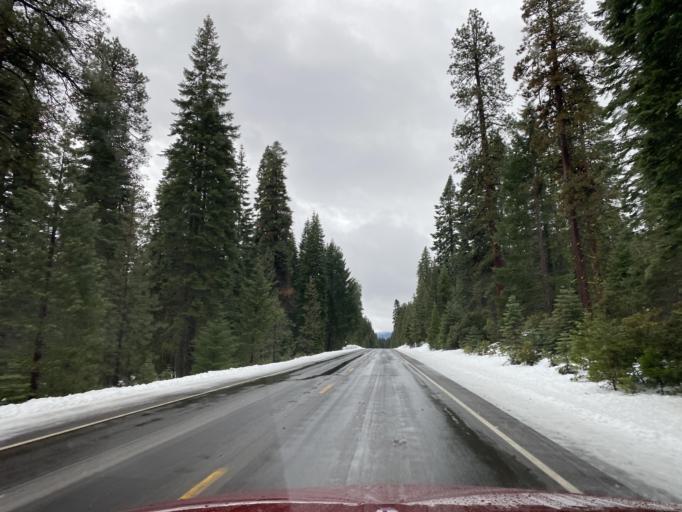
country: US
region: Oregon
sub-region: Klamath County
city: Klamath Falls
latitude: 42.5148
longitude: -122.0836
